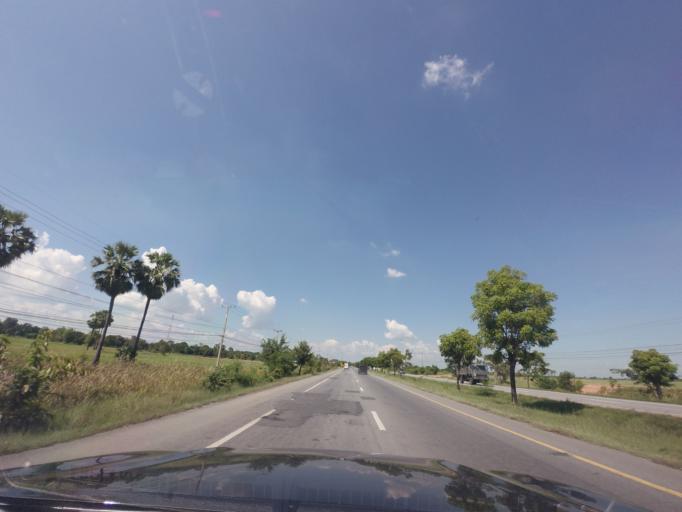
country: TH
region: Nakhon Ratchasima
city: Non Sung
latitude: 15.1779
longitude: 102.3375
